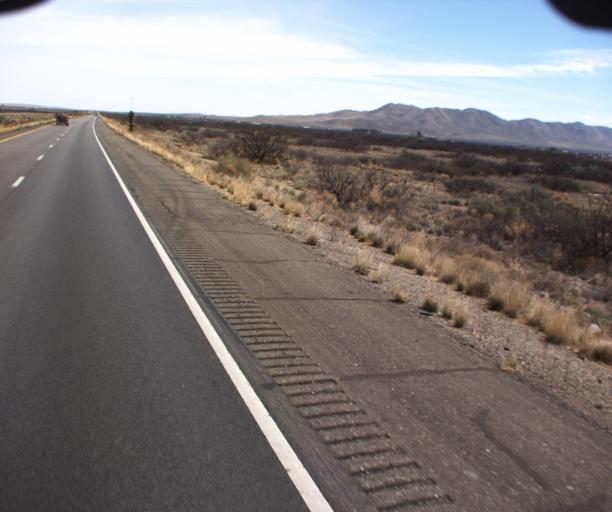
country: US
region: Arizona
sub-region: Cochise County
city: Willcox
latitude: 32.2789
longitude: -109.8322
